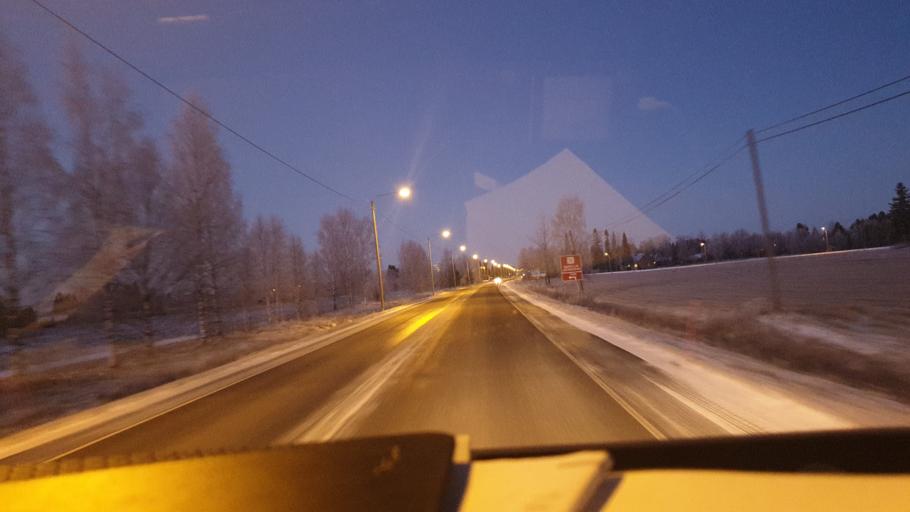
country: FI
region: Northern Ostrobothnia
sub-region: Raahe
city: Raahe
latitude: 64.6882
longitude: 24.6017
